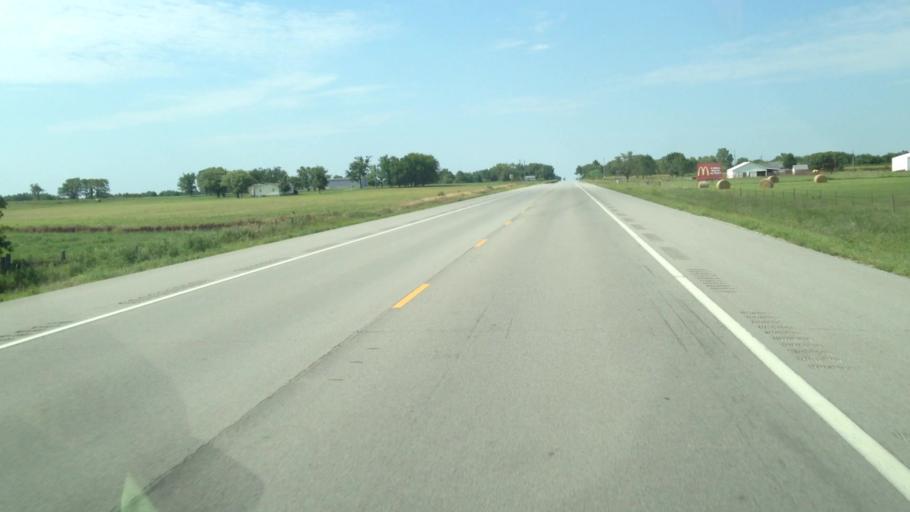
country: US
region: Kansas
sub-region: Labette County
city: Altamont
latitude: 37.2480
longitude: -95.2670
